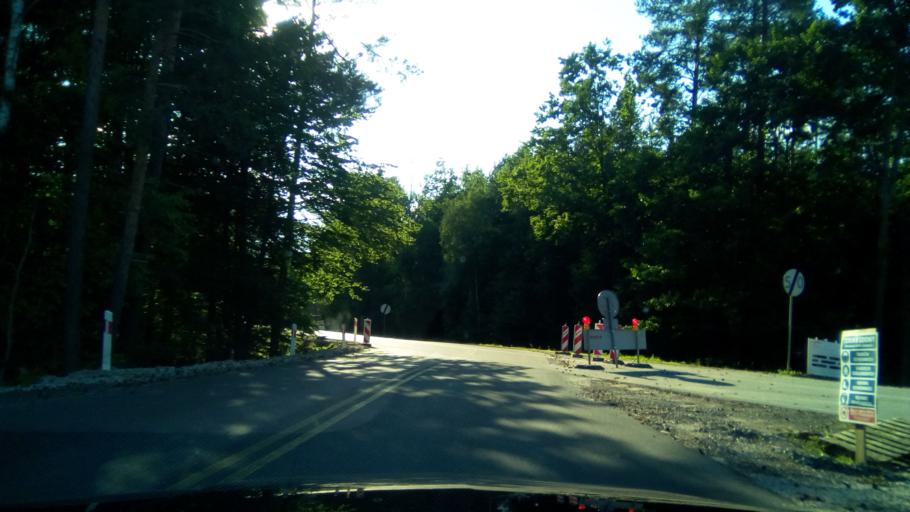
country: PL
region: Masovian Voivodeship
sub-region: Powiat bialobrzeski
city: Stromiec
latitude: 51.6422
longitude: 21.1743
